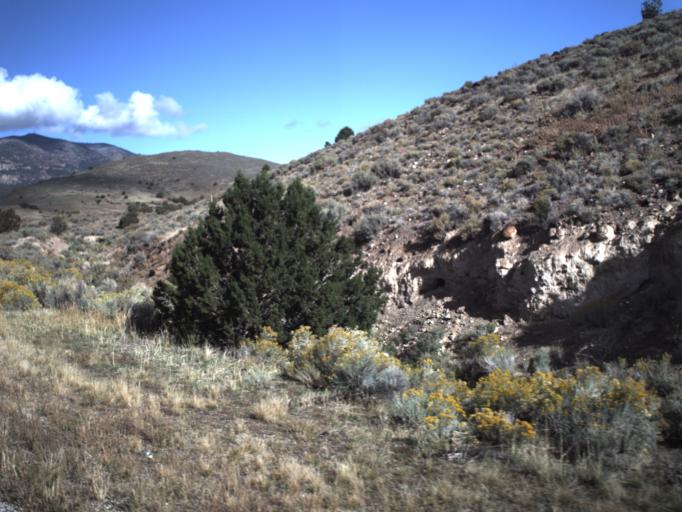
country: US
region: Utah
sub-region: Beaver County
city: Milford
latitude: 38.4591
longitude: -113.2318
